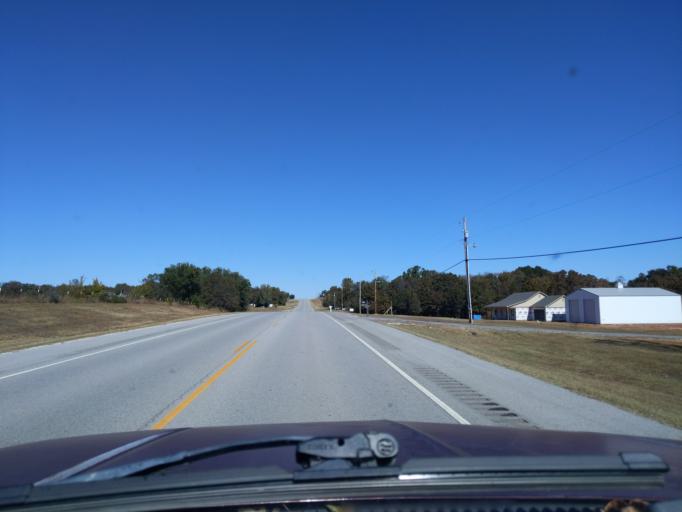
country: US
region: Oklahoma
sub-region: Creek County
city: Bristow
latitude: 35.7630
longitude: -96.3872
